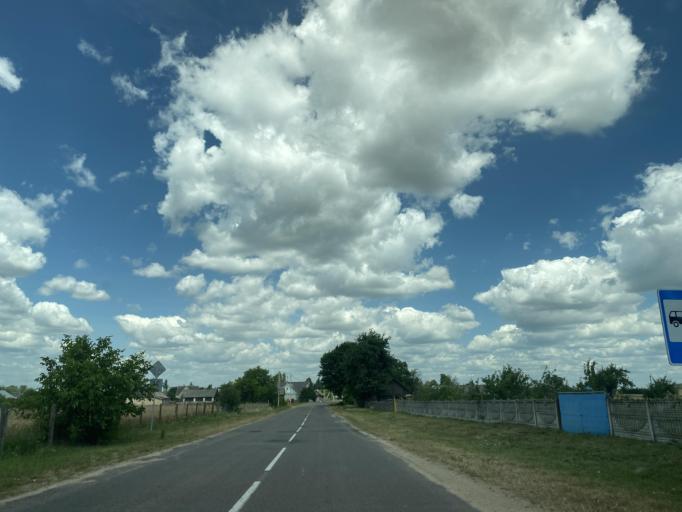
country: BY
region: Brest
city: Ivanava
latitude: 52.1679
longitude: 25.5590
